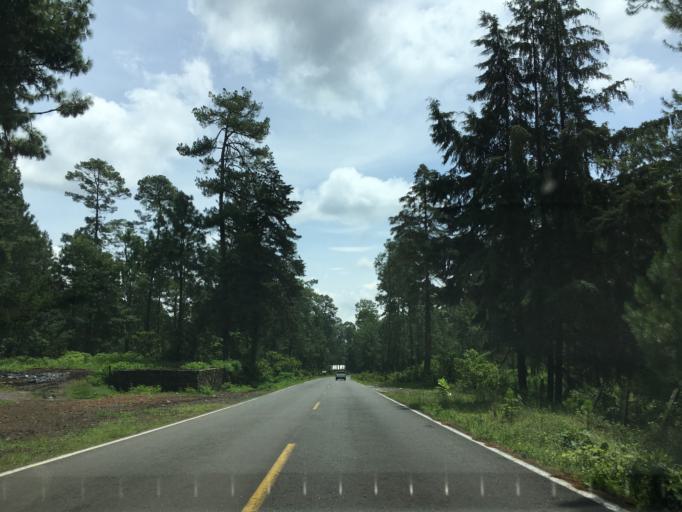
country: MX
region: Michoacan
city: Nuevo San Juan Parangaricutiro
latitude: 19.4434
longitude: -102.1596
